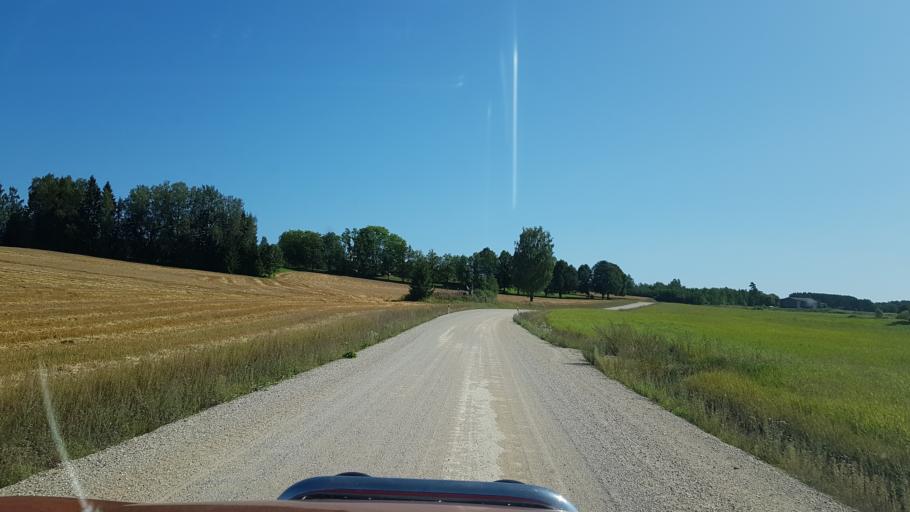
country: EE
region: Vorumaa
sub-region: Voru linn
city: Voru
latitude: 57.7361
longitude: 27.2453
